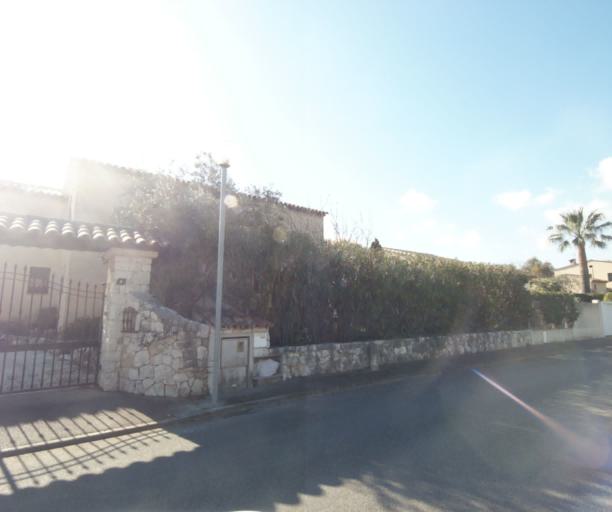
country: FR
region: Provence-Alpes-Cote d'Azur
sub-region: Departement des Alpes-Maritimes
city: Biot
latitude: 43.6163
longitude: 7.1205
